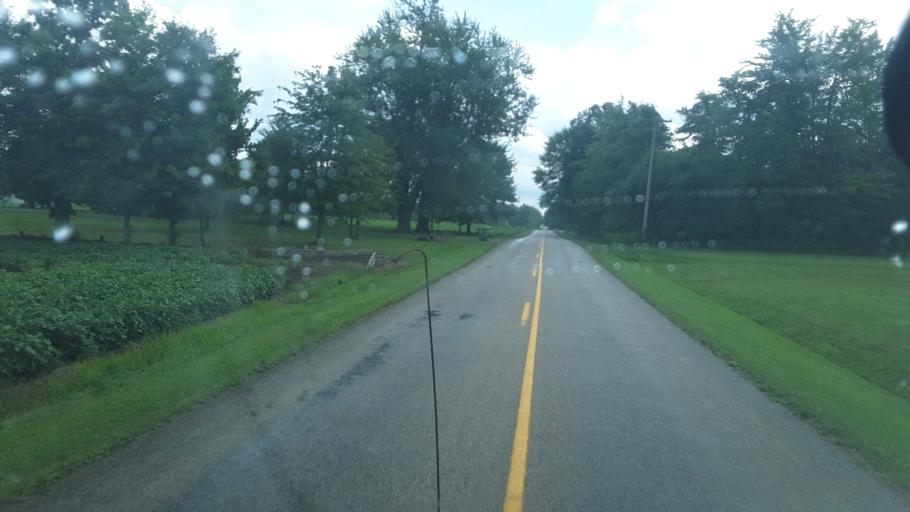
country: US
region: Ohio
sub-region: Ashtabula County
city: Roaming Shores
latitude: 41.6203
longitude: -80.7219
